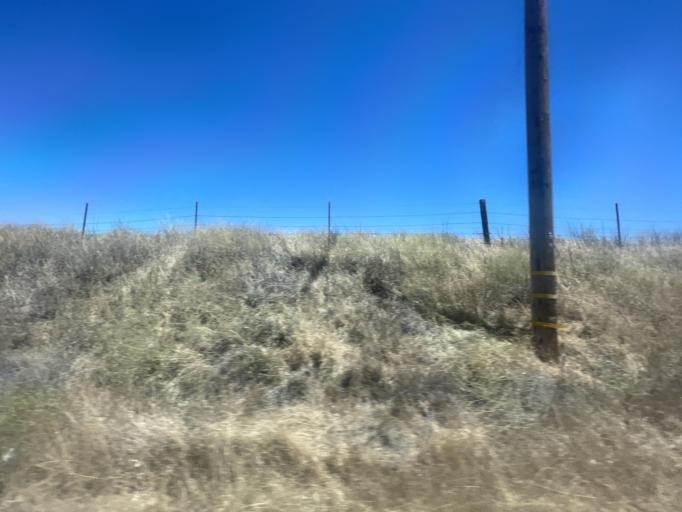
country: US
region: California
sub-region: San Luis Obispo County
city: Paso Robles
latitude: 35.6368
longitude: -120.5985
